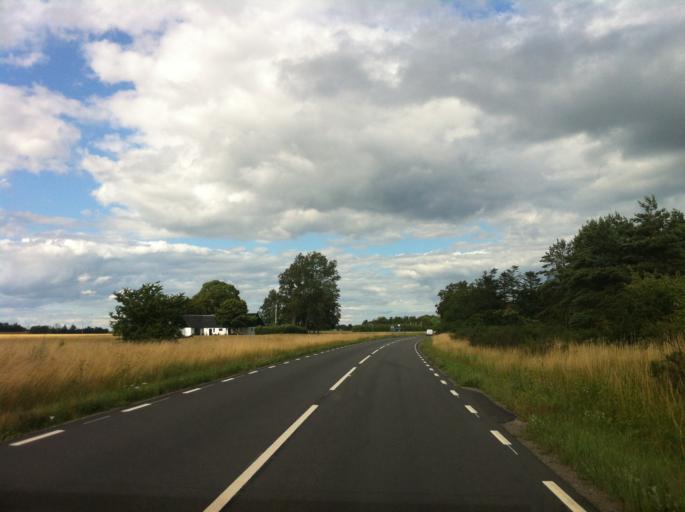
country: SE
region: Skane
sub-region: Simrishamns Kommun
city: Simrishamn
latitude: 55.3934
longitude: 14.1734
